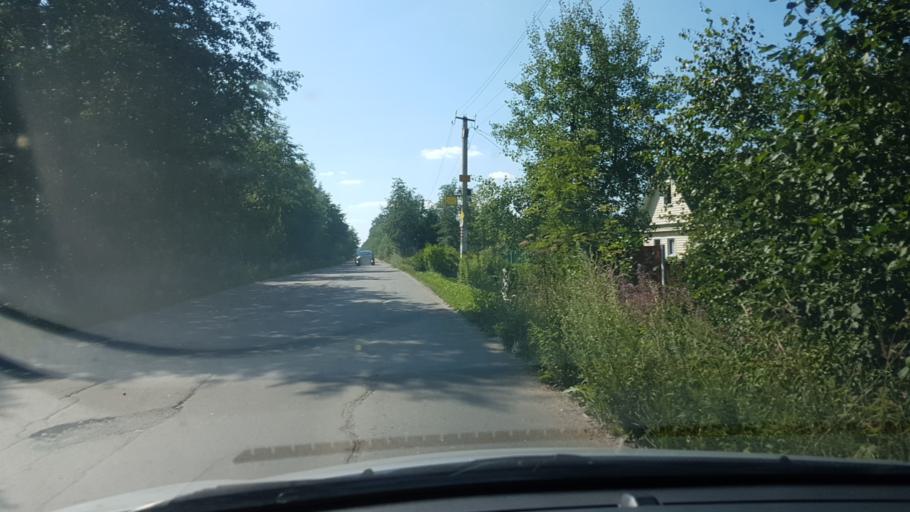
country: RU
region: Leningrad
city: Vyritsa
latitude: 59.4484
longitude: 30.3028
